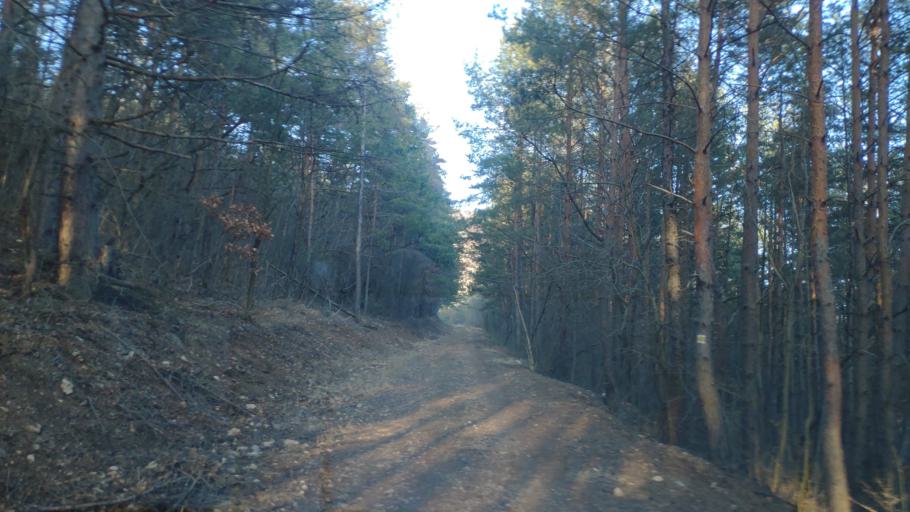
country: SK
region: Kosicky
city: Medzev
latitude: 48.6062
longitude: 20.7366
